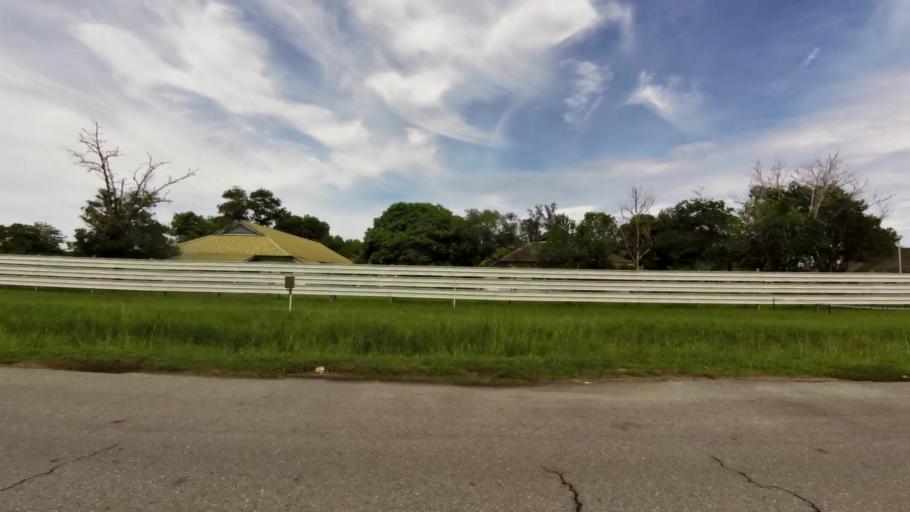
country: BN
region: Belait
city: Seria
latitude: 4.6063
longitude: 114.3085
